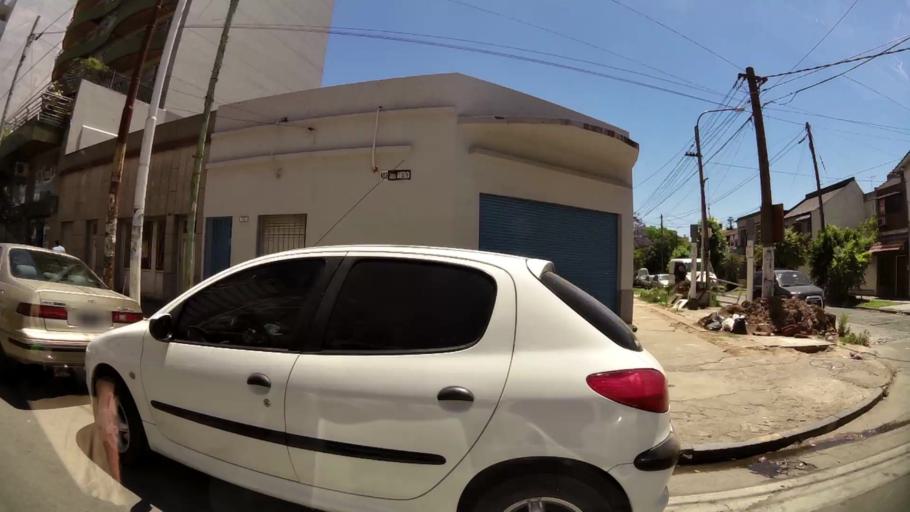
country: AR
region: Buenos Aires
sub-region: Partido de General San Martin
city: General San Martin
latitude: -34.6010
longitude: -58.5262
